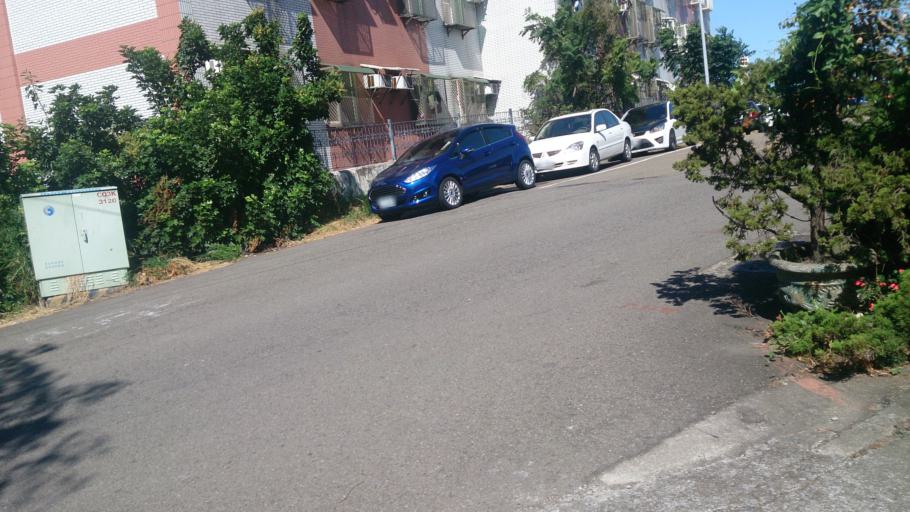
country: TW
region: Taiwan
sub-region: Hsinchu
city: Hsinchu
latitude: 24.7531
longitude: 120.9520
